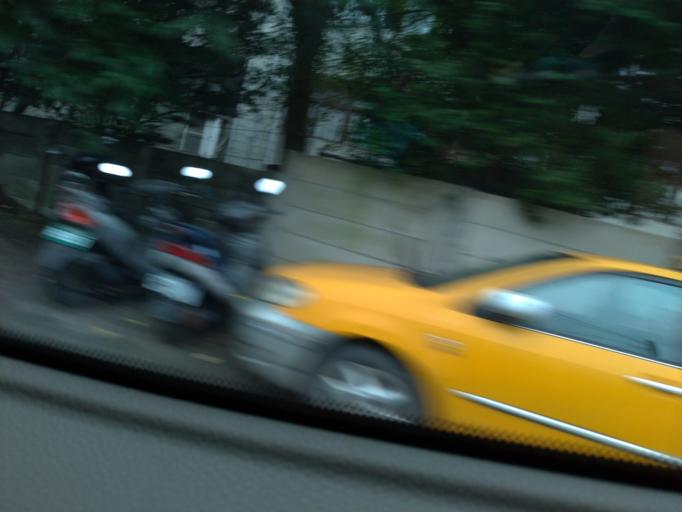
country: TW
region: Taipei
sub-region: Taipei
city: Banqiao
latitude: 24.9285
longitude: 121.4125
